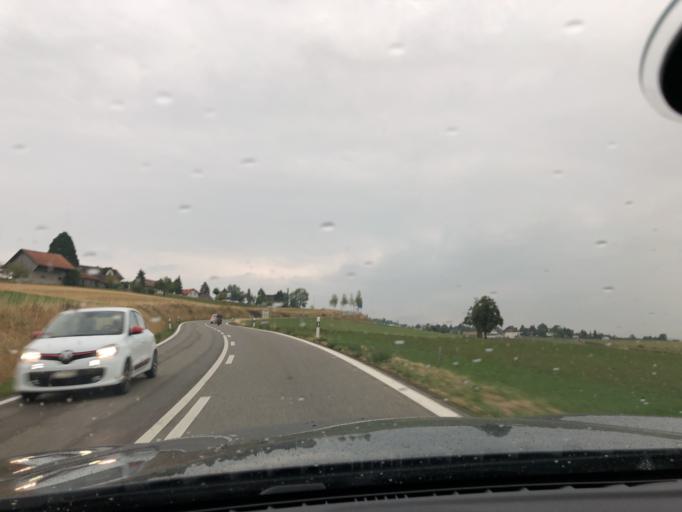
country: CH
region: Aargau
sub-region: Bezirk Bremgarten
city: Berikon
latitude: 47.3452
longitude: 8.3761
